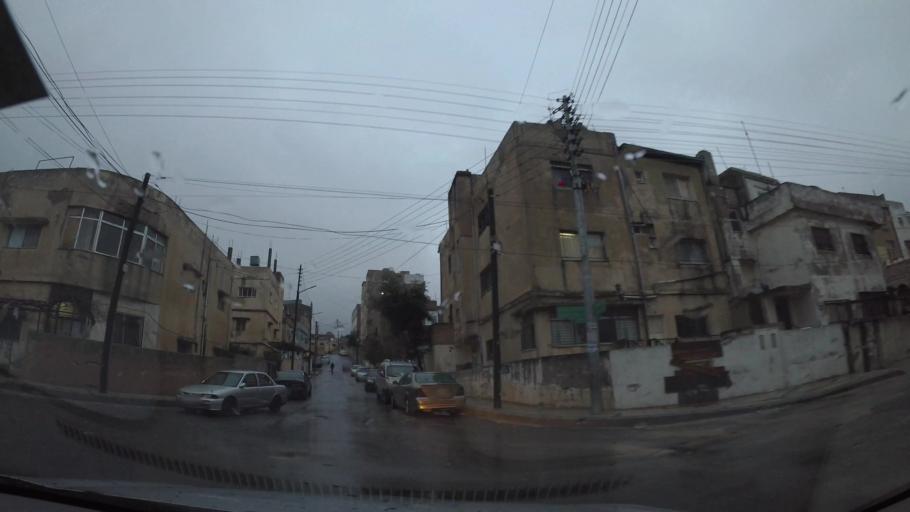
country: JO
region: Amman
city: Al Jubayhah
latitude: 32.0281
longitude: 35.8449
